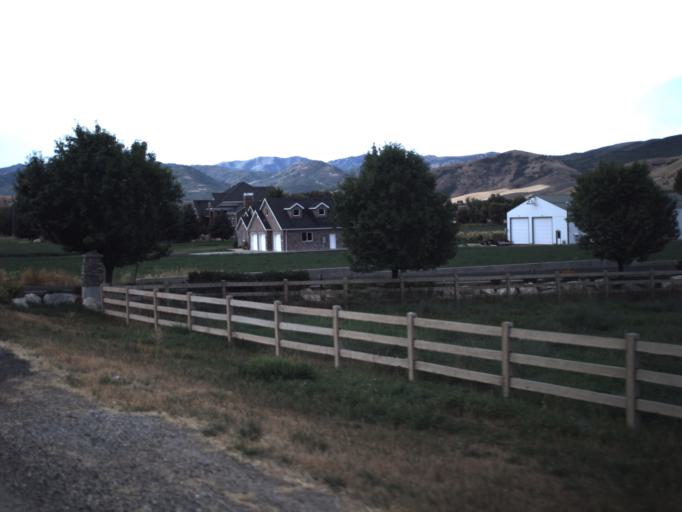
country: US
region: Utah
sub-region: Morgan County
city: Morgan
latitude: 41.0141
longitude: -111.6766
